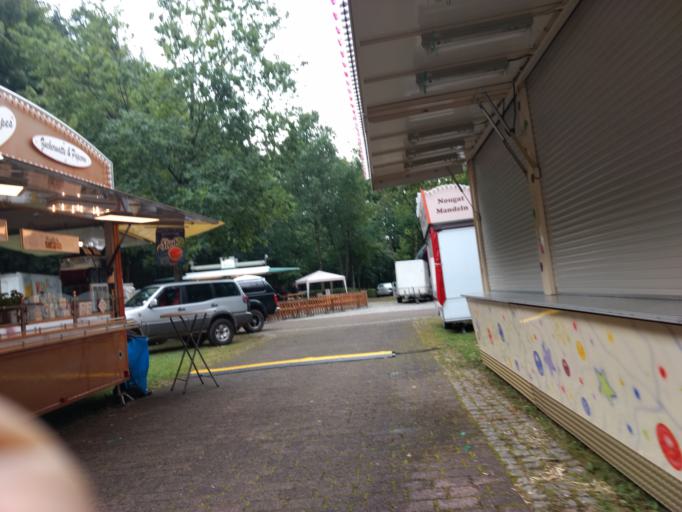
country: DE
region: Saarland
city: Nalbach
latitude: 49.3935
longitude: 6.8016
